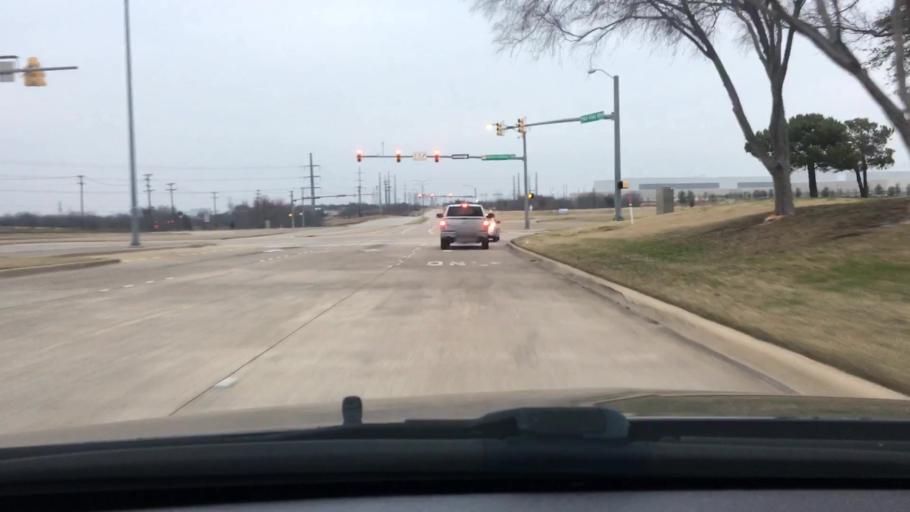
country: US
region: Texas
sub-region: Denton County
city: Roanoke
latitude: 32.9782
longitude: -97.2627
